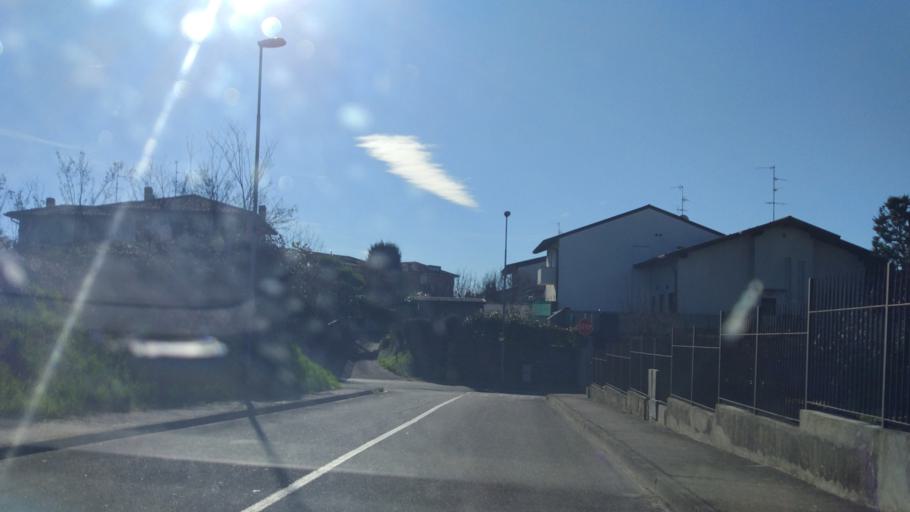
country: IT
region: Lombardy
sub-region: Provincia di Monza e Brianza
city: Giussano
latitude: 45.7021
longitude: 9.2142
